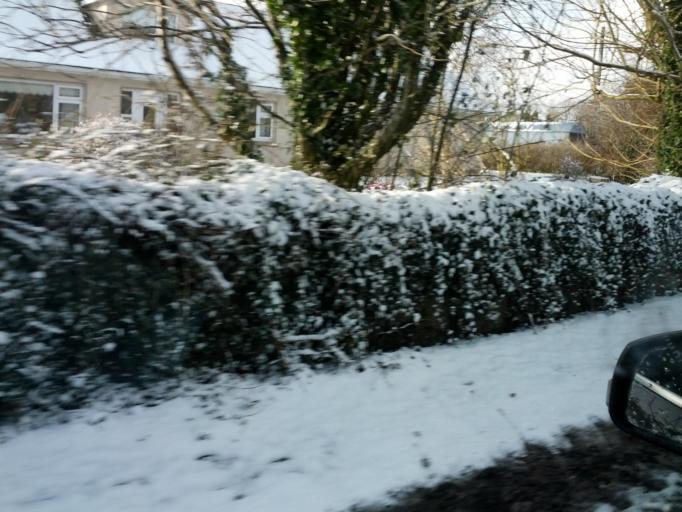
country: IE
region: Connaught
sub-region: County Galway
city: Athenry
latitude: 53.2010
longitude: -8.7610
